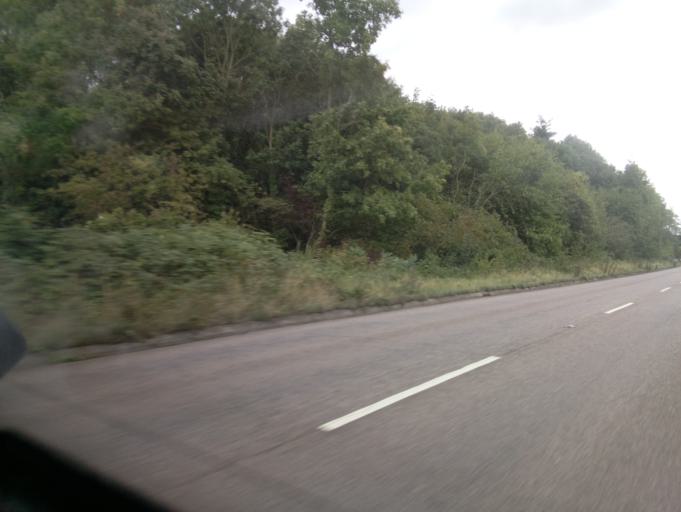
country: GB
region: England
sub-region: Devon
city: Exminster
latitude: 50.6834
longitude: -3.4911
